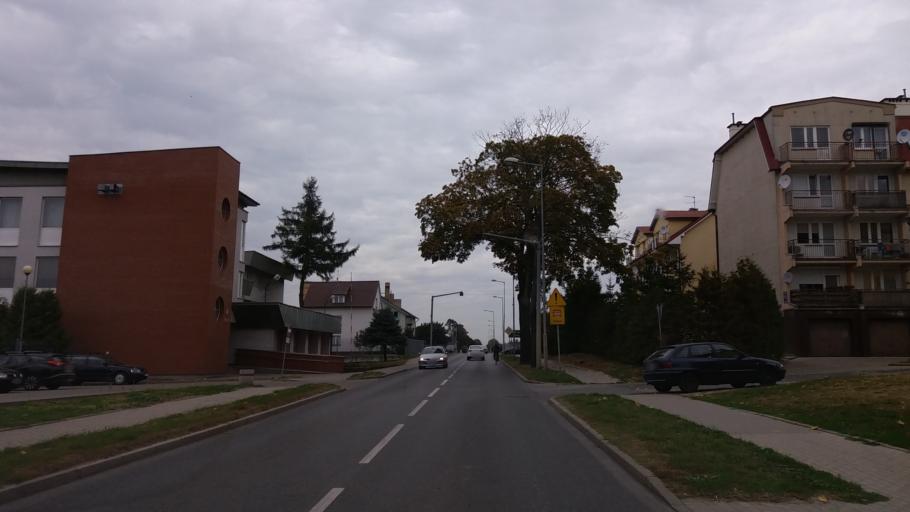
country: PL
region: Lubusz
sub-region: Powiat strzelecko-drezdenecki
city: Strzelce Krajenskie
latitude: 52.8808
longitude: 15.5233
